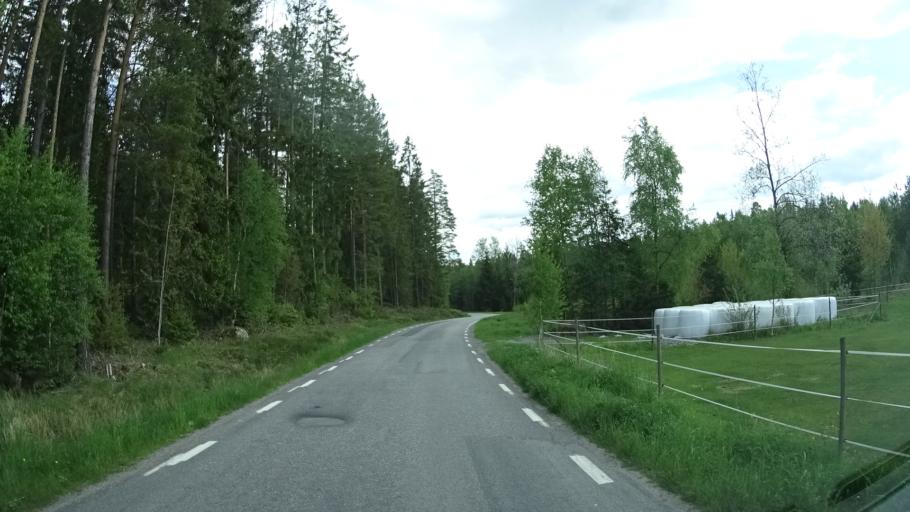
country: SE
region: OEstergoetland
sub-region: Finspangs Kommun
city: Finspang
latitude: 58.6011
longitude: 15.7603
